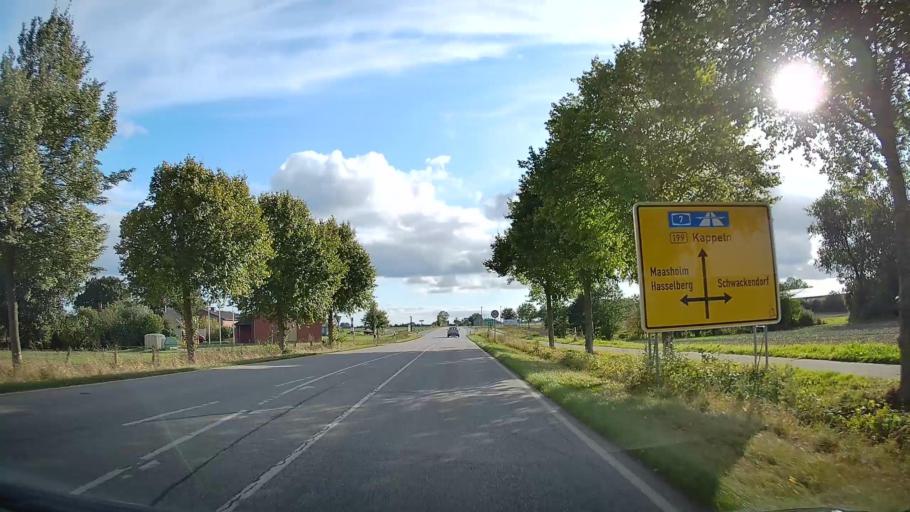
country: DE
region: Schleswig-Holstein
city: Rabel
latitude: 54.7134
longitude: 9.9504
